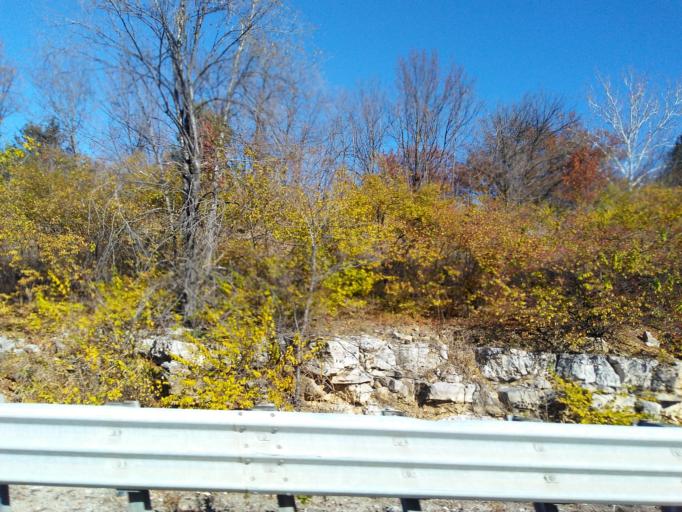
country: US
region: Missouri
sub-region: Saint Louis County
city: Concord
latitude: 38.5103
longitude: -90.3600
